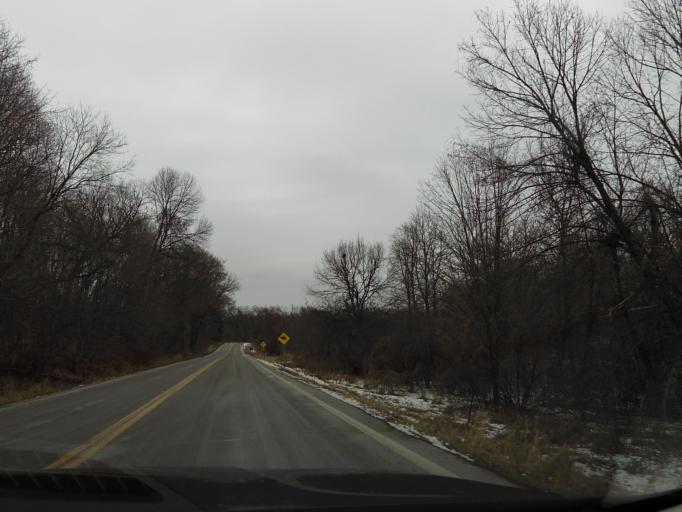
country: US
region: Minnesota
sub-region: Hennepin County
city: Medina
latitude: 45.0077
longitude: -93.6059
